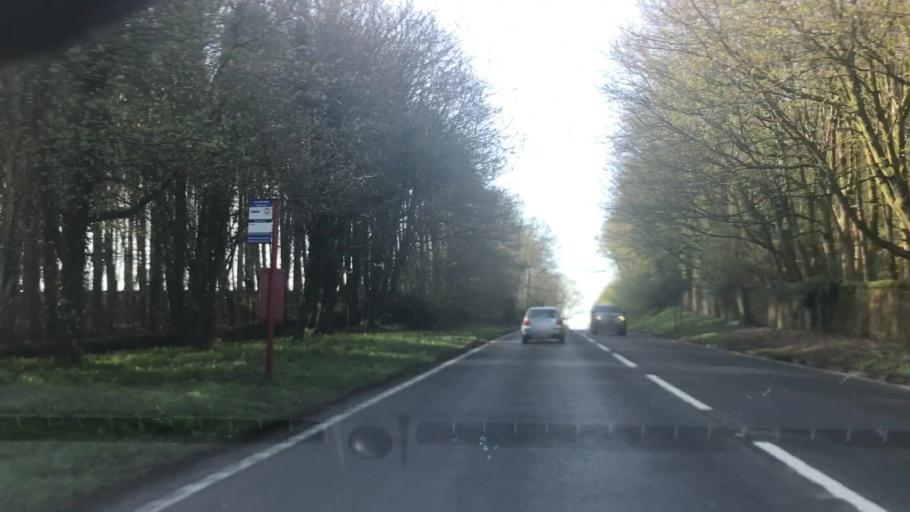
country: GB
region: England
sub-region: City and Borough of Leeds
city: Shadwell
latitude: 53.8831
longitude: -1.5065
